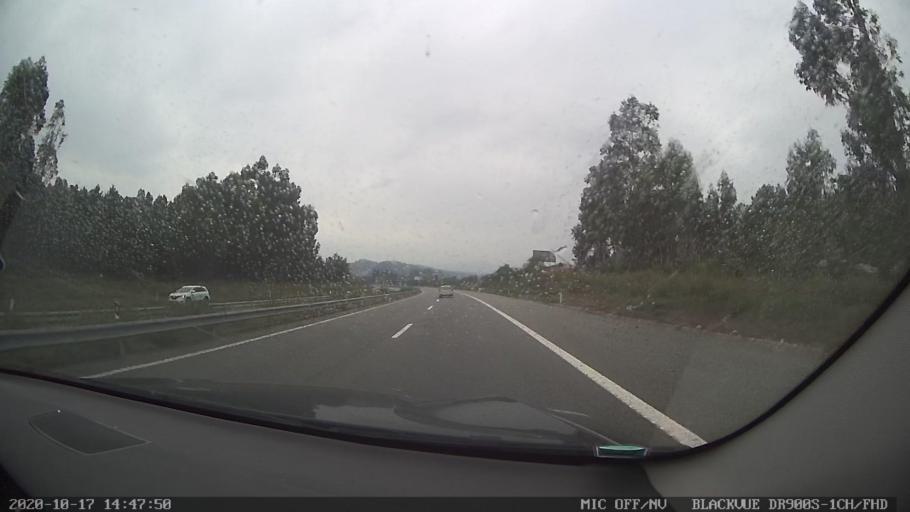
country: PT
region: Braga
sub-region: Barcelos
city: Galegos
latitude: 41.5385
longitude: -8.5312
